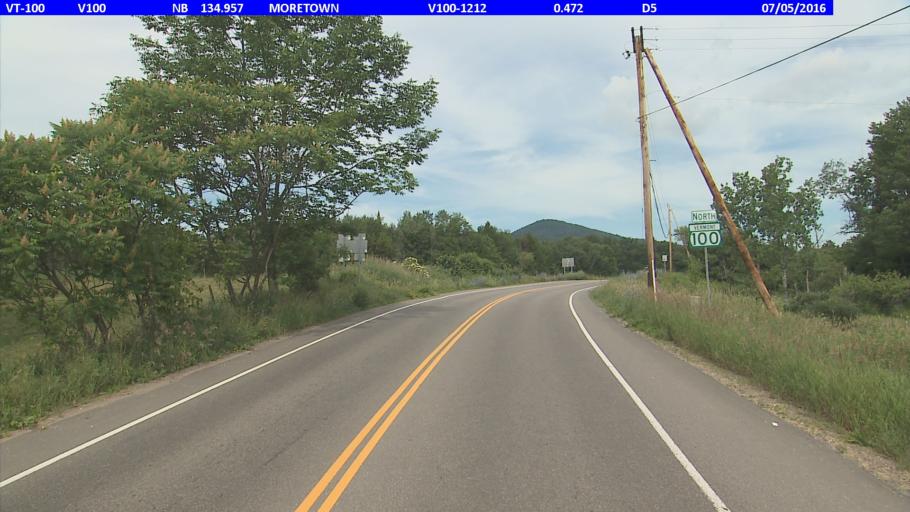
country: US
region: Vermont
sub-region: Washington County
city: Waterbury
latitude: 44.2404
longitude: -72.7757
